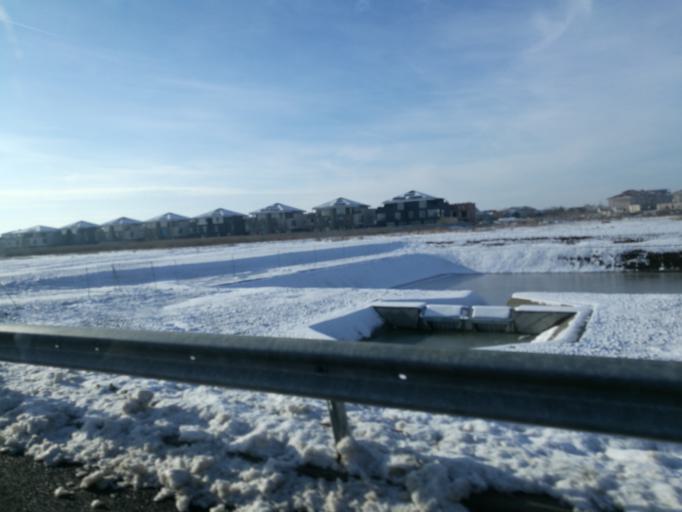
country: RO
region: Ilfov
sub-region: Voluntari City
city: Voluntari
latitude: 44.4951
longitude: 26.1506
